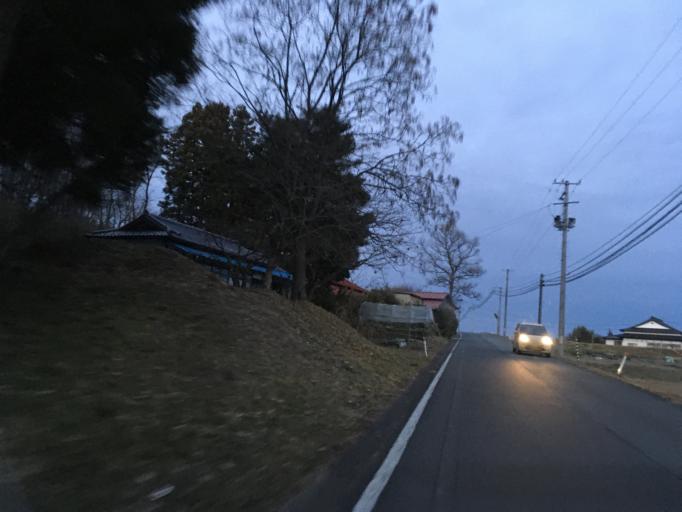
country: JP
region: Miyagi
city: Kogota
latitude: 38.6806
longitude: 141.0937
